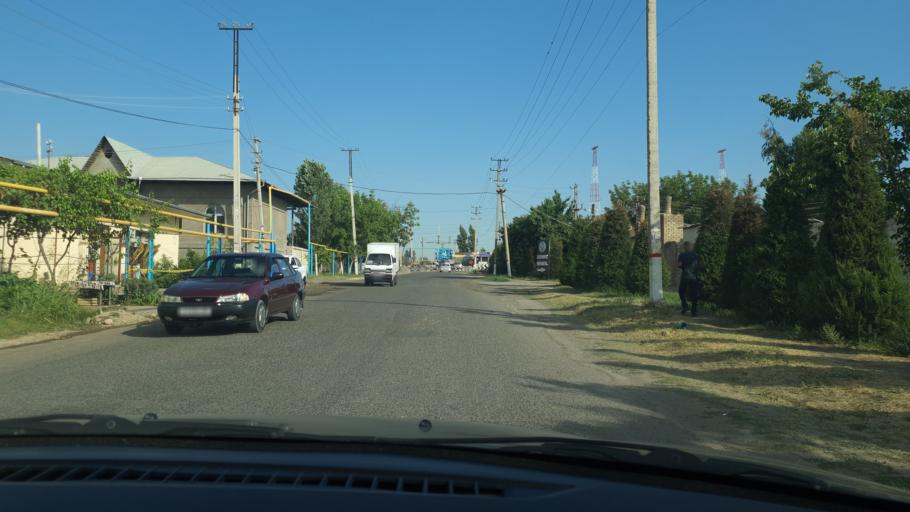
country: UZ
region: Toshkent
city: Urtaowul
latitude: 41.2067
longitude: 69.1490
